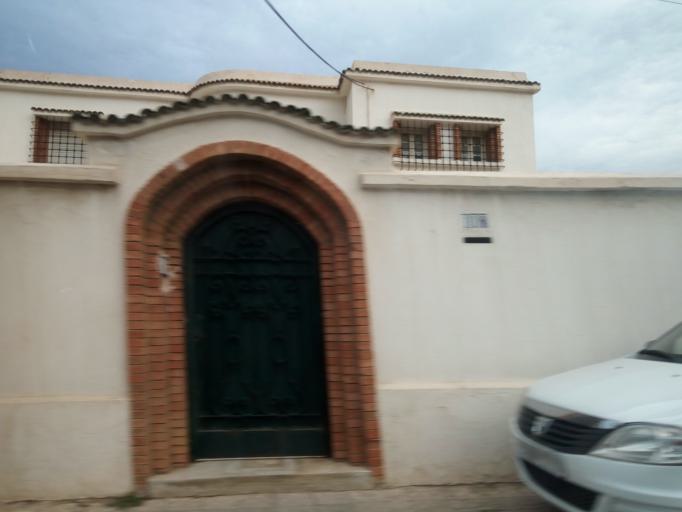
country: DZ
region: Tipaza
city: Cheraga
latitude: 36.8148
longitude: 2.9961
